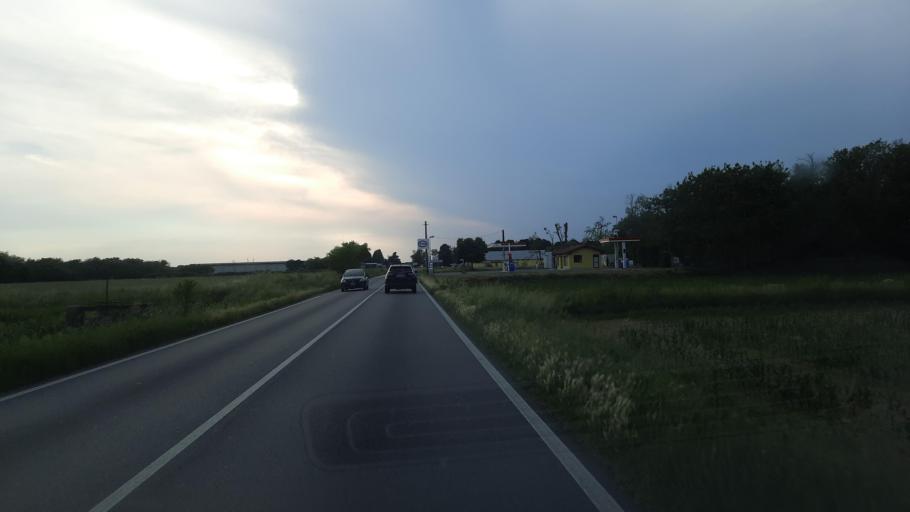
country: IT
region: Lombardy
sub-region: Provincia di Pavia
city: Villanova d'Ardenghi
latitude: 45.1625
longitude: 9.0273
